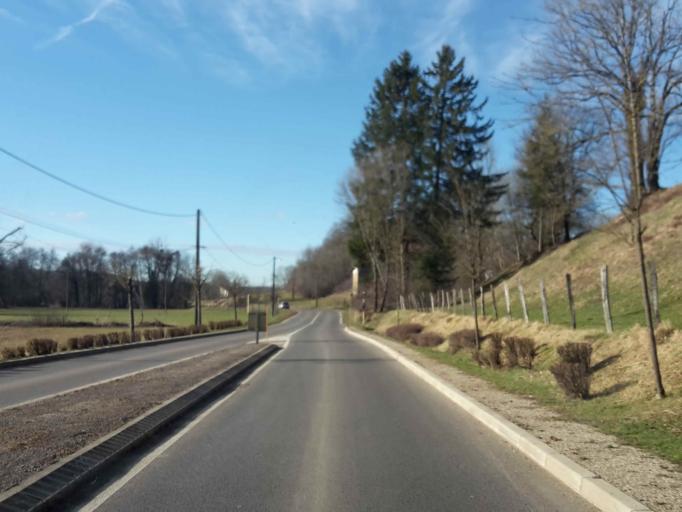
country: FR
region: Franche-Comte
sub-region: Departement du Doubs
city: Vercel-Villedieu-le-Camp
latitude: 47.2335
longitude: 6.3978
